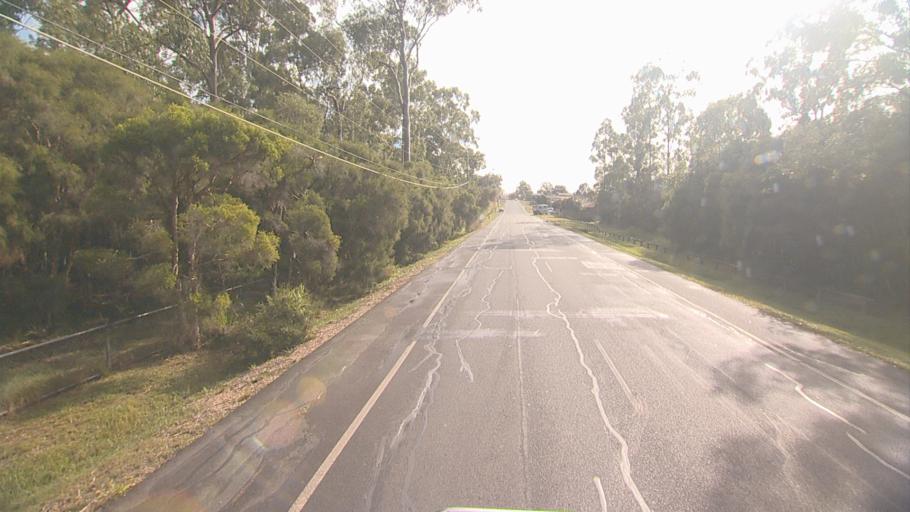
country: AU
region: Queensland
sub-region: Logan
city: Waterford West
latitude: -27.6883
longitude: 153.1120
